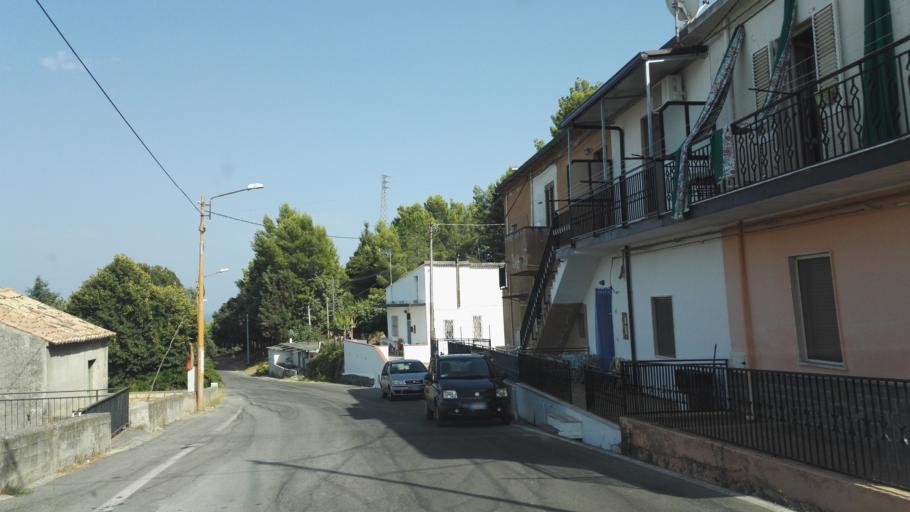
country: IT
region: Calabria
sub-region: Provincia di Reggio Calabria
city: Monasterace
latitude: 38.4545
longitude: 16.5529
